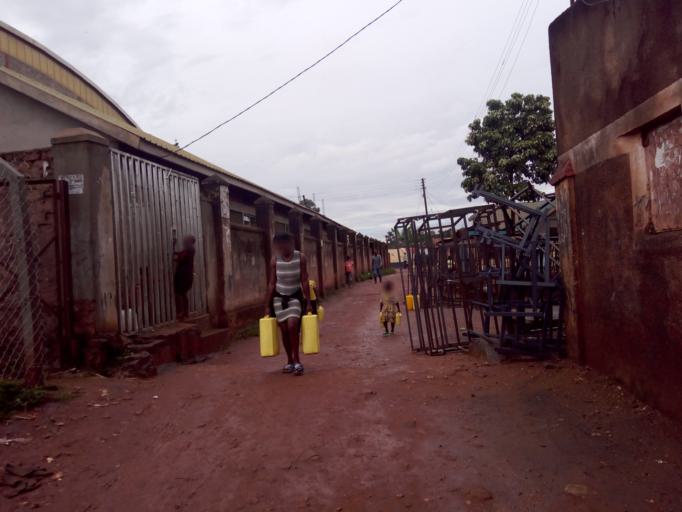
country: UG
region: Central Region
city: Kampala Central Division
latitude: 0.3313
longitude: 32.5614
